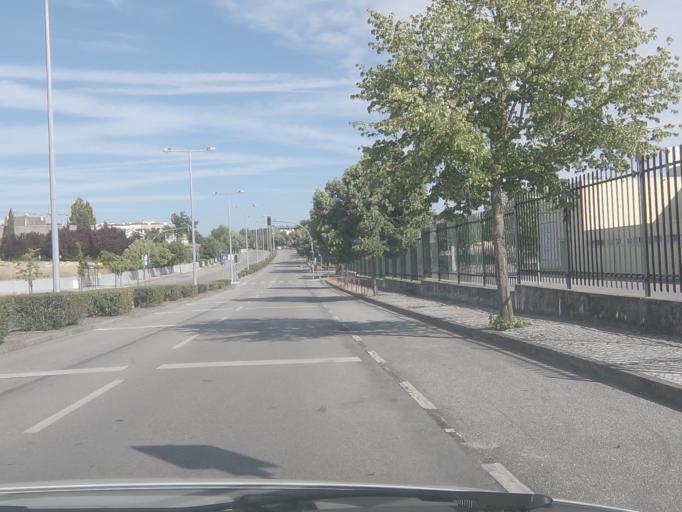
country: PT
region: Viseu
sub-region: Viseu
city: Viseu
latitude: 40.6432
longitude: -7.9215
